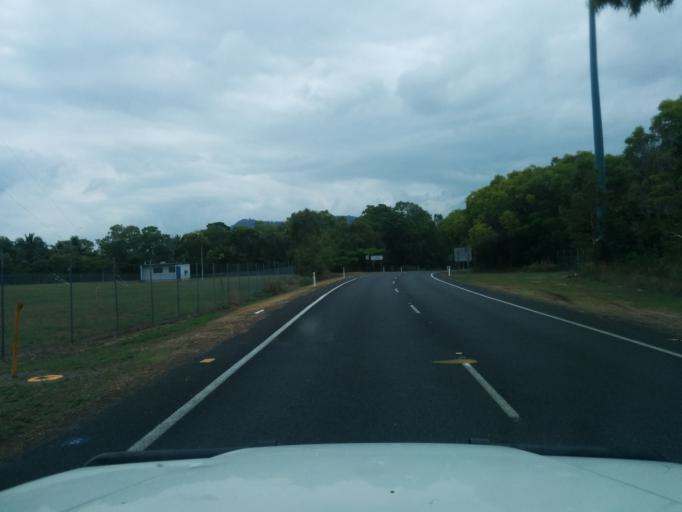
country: AU
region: Queensland
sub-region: Cairns
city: Yorkeys Knob
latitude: -16.8464
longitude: 145.7350
